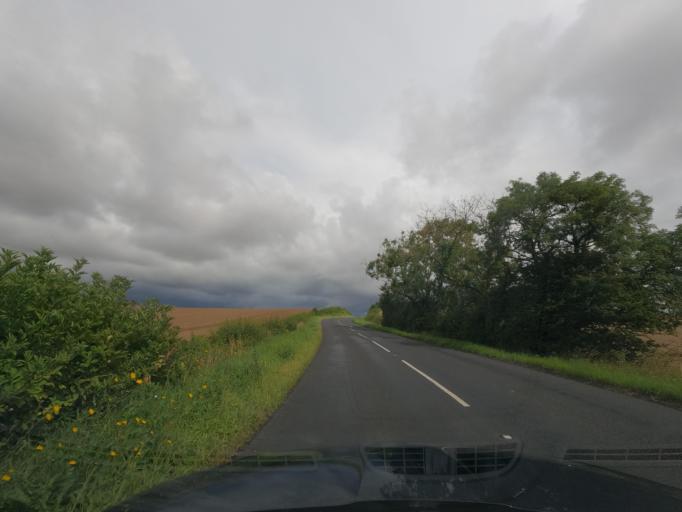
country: GB
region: England
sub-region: Northumberland
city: Ancroft
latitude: 55.7075
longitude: -1.9956
